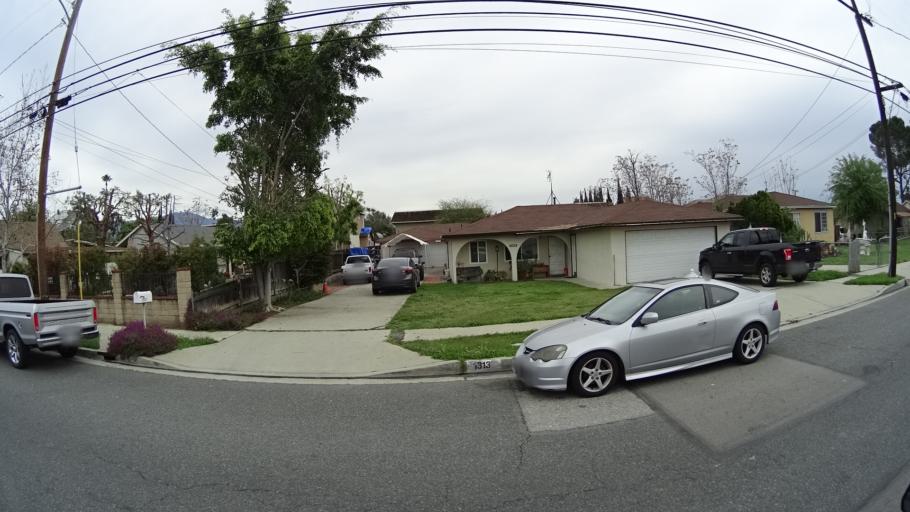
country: US
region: California
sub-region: Los Angeles County
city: West Puente Valley
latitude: 34.0690
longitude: -117.9873
